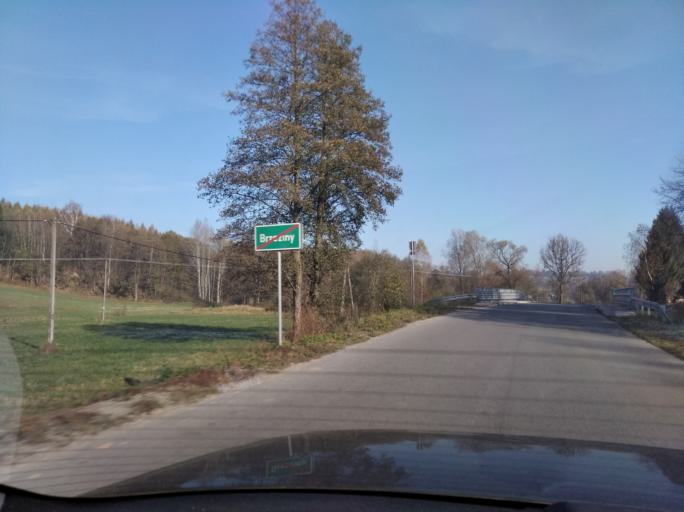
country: PL
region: Subcarpathian Voivodeship
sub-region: Powiat ropczycko-sedziszowski
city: Wielopole Skrzynskie
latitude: 49.9473
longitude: 21.5889
